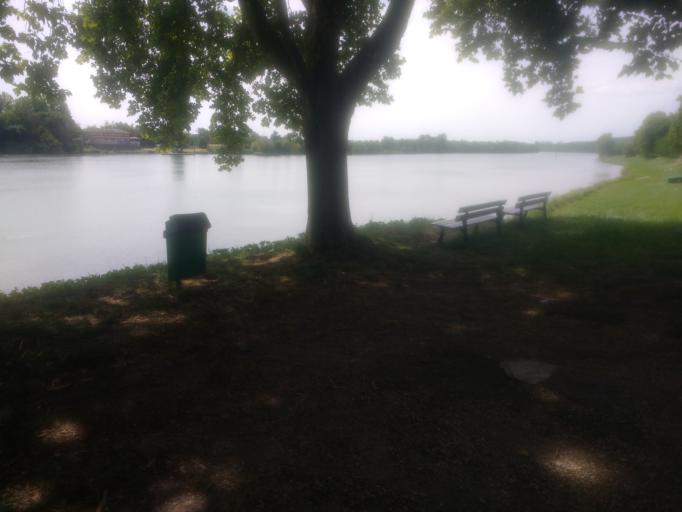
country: FR
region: Bourgogne
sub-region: Departement de Saone-et-Loire
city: Saint-Martin-Belle-Roche
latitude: 46.3650
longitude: 4.8549
